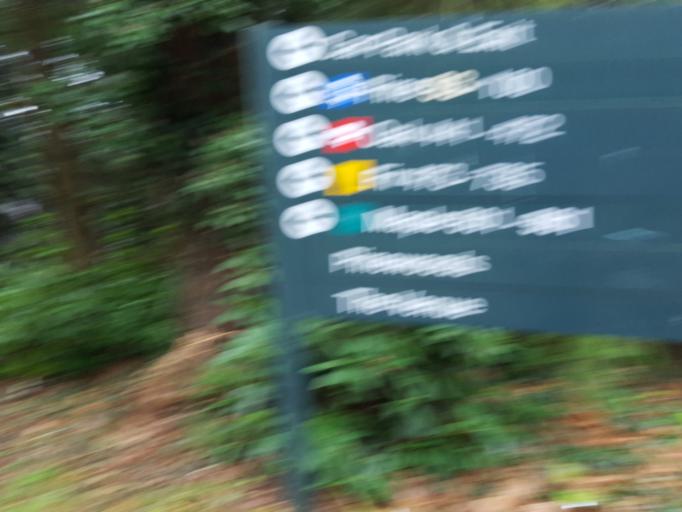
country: GB
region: England
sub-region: Wiltshire
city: Corsley
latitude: 51.1867
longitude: -2.2292
